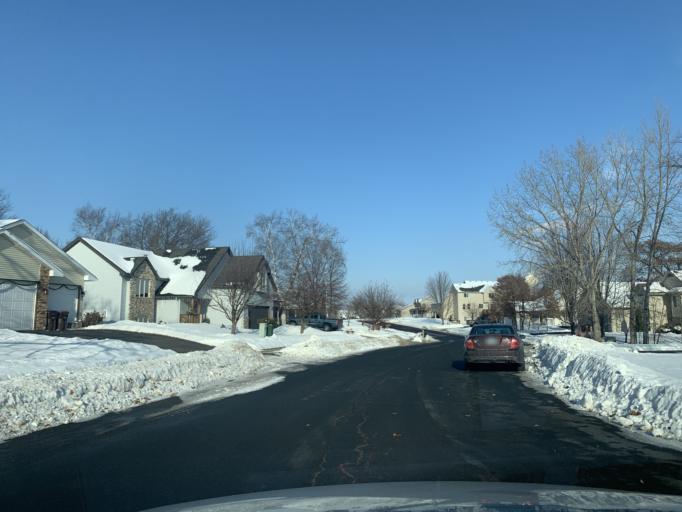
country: US
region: Minnesota
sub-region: Wright County
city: Buffalo
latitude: 45.2041
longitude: -93.8340
